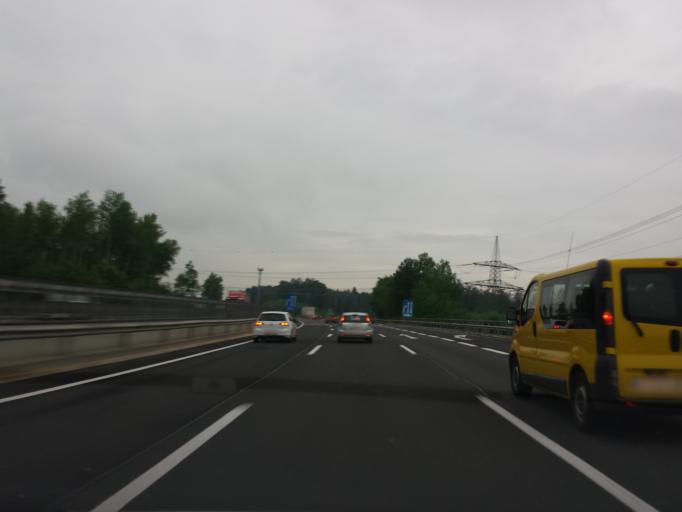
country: AT
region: Styria
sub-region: Politischer Bezirk Weiz
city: Nitscha
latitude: 47.1054
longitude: 15.7720
